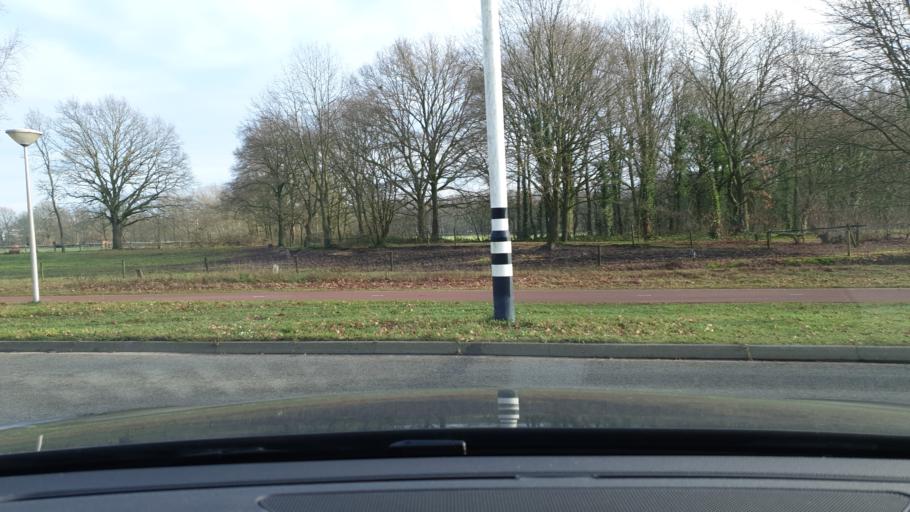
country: NL
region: North Brabant
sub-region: Gemeente Waalre
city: Waalre
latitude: 51.4116
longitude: 5.4636
